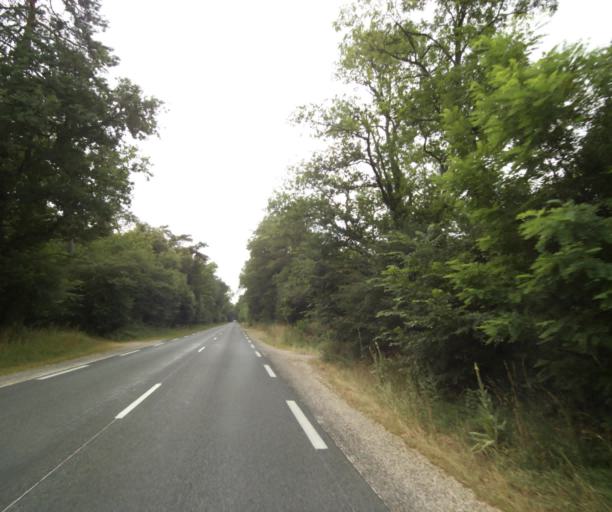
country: FR
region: Ile-de-France
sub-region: Departement de Seine-et-Marne
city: Arbonne-la-Foret
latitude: 48.4155
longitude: 2.5944
